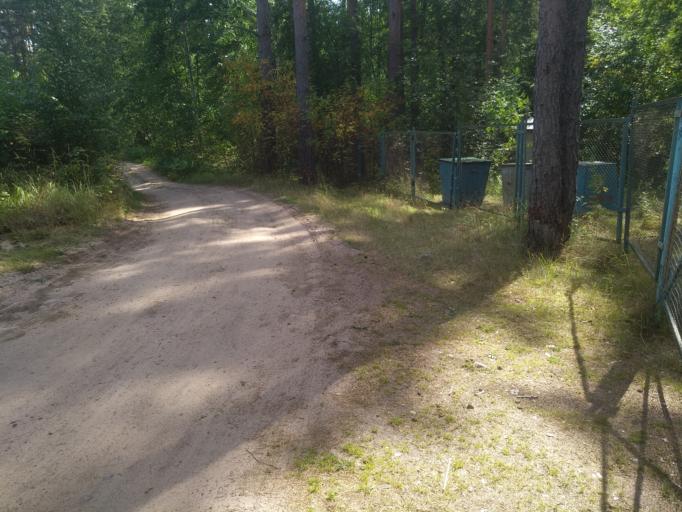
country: RU
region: Leningrad
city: Sapernoye
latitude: 60.6799
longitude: 29.9075
